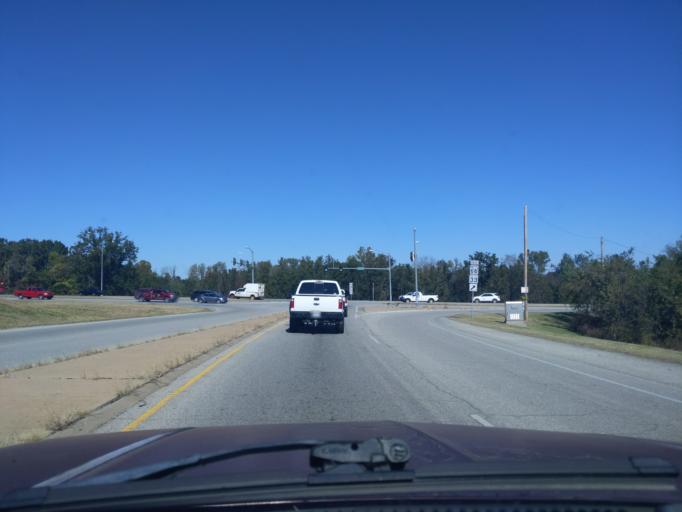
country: US
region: Oklahoma
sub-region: Creek County
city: Sapulpa
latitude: 35.9919
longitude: -96.1411
